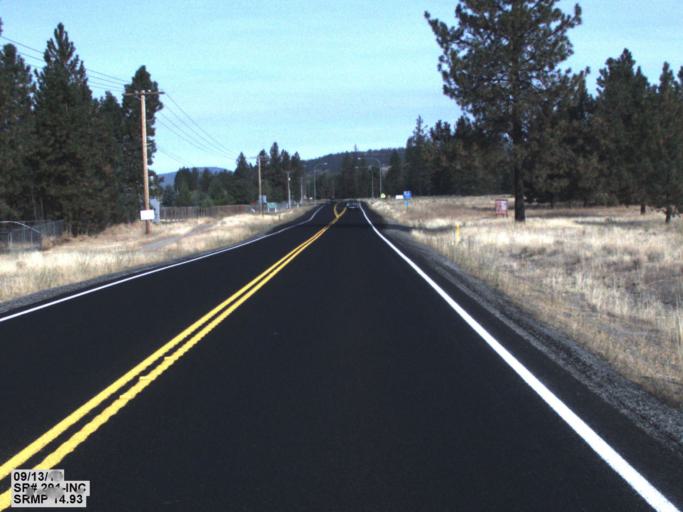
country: US
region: Washington
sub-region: Spokane County
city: Deer Park
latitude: 47.8266
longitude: -117.5948
